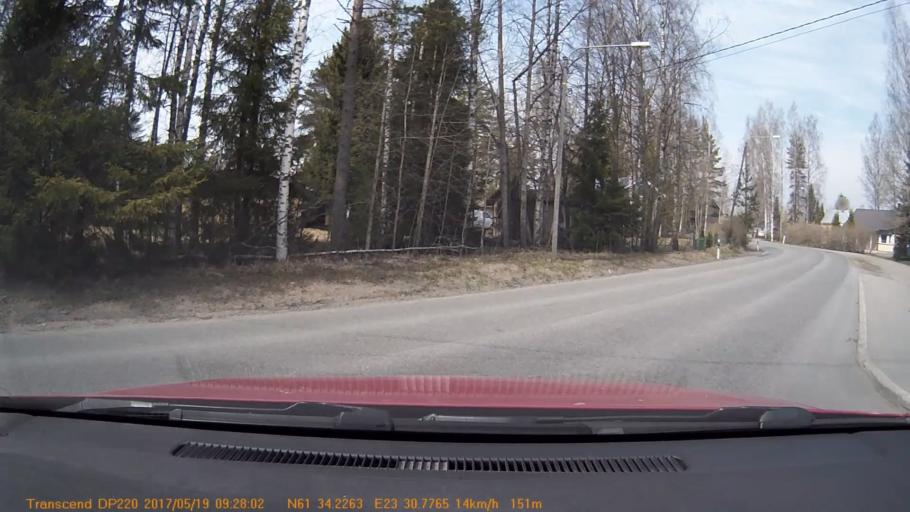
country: FI
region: Pirkanmaa
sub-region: Tampere
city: Yloejaervi
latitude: 61.5699
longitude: 23.5134
